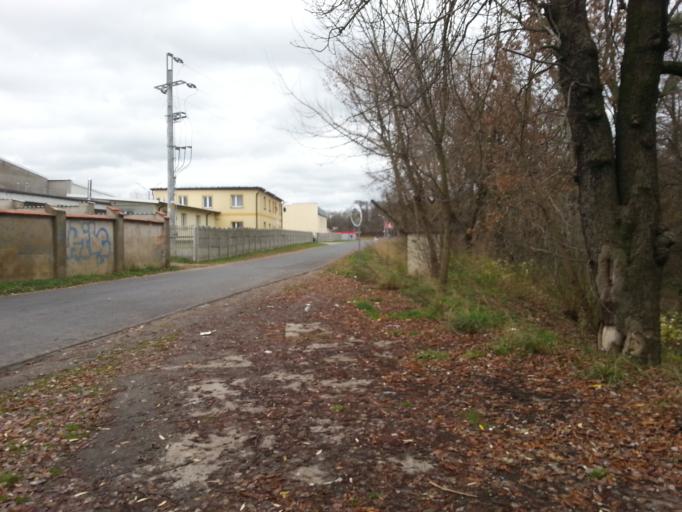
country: PL
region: Lower Silesian Voivodeship
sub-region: Powiat olesnicki
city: Twardogora
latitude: 51.3640
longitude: 17.4734
